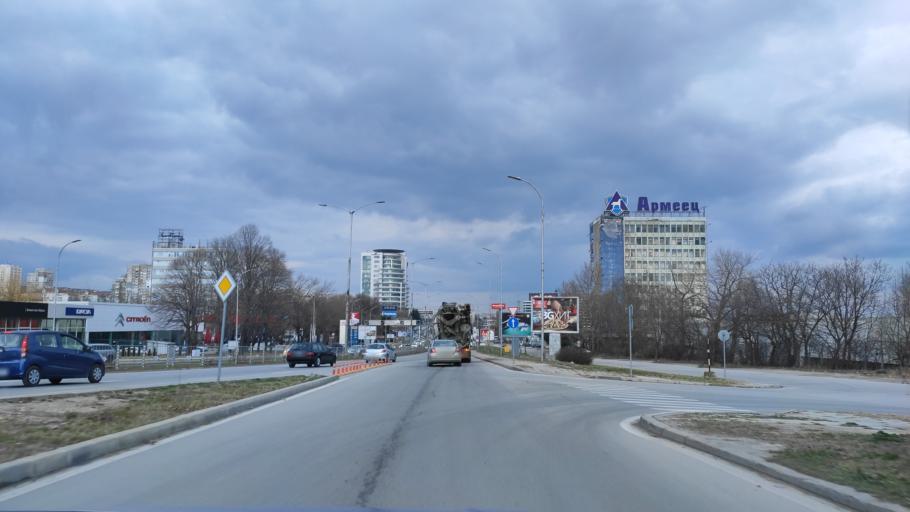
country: BG
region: Varna
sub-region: Obshtina Varna
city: Varna
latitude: 43.2228
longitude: 27.8692
